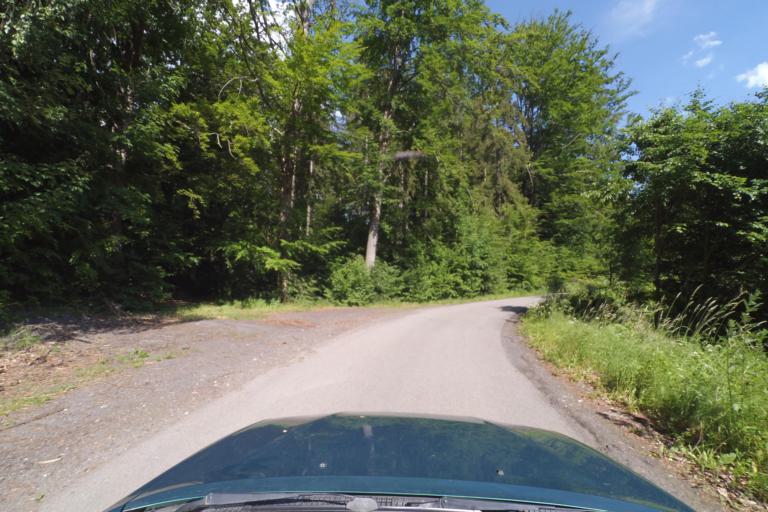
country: CZ
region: Liberecky
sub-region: Okres Ceska Lipa
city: Straz pod Ralskem
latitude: 50.6725
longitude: 14.8584
